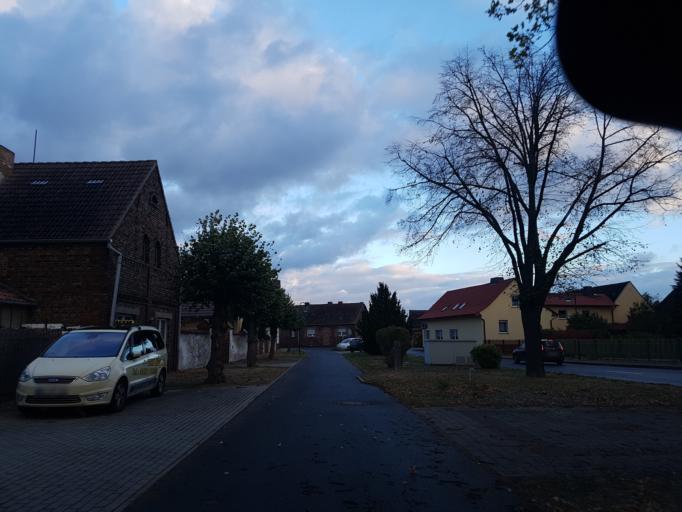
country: DE
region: Saxony-Anhalt
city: Annaburg
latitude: 51.7833
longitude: 13.0652
